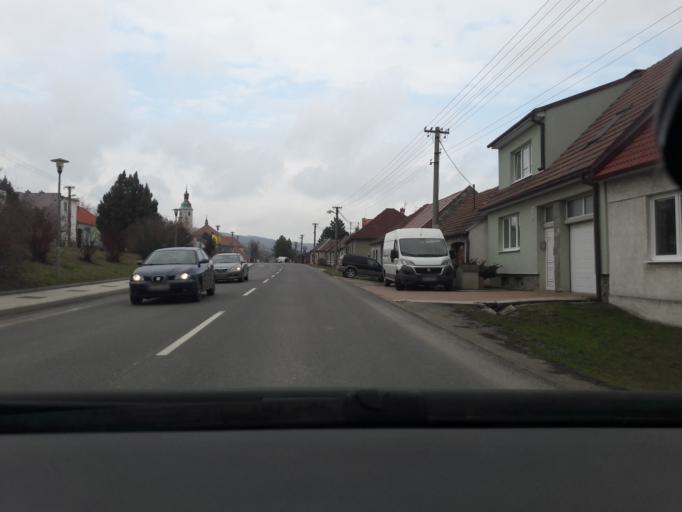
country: SK
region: Bratislavsky
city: Modra
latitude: 48.3973
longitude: 17.3563
